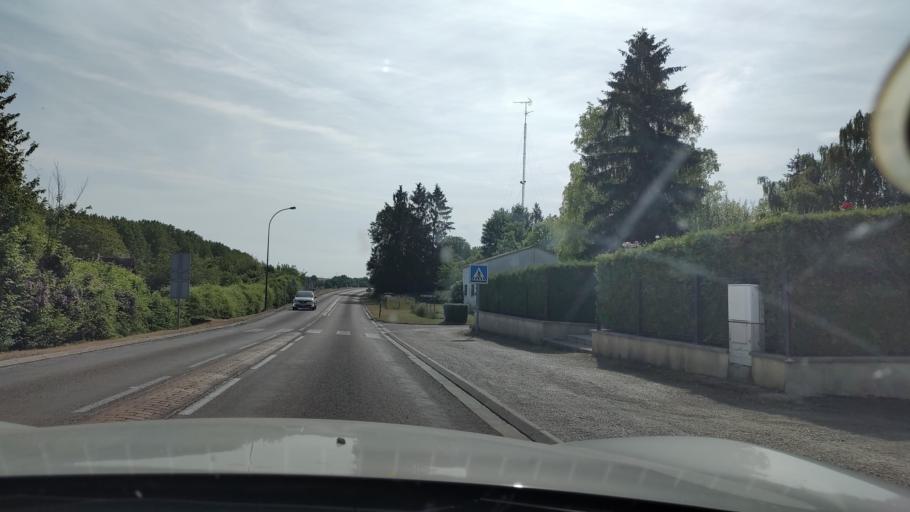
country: FR
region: Champagne-Ardenne
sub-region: Departement de l'Aube
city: Nogent-sur-Seine
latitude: 48.4479
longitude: 3.6191
